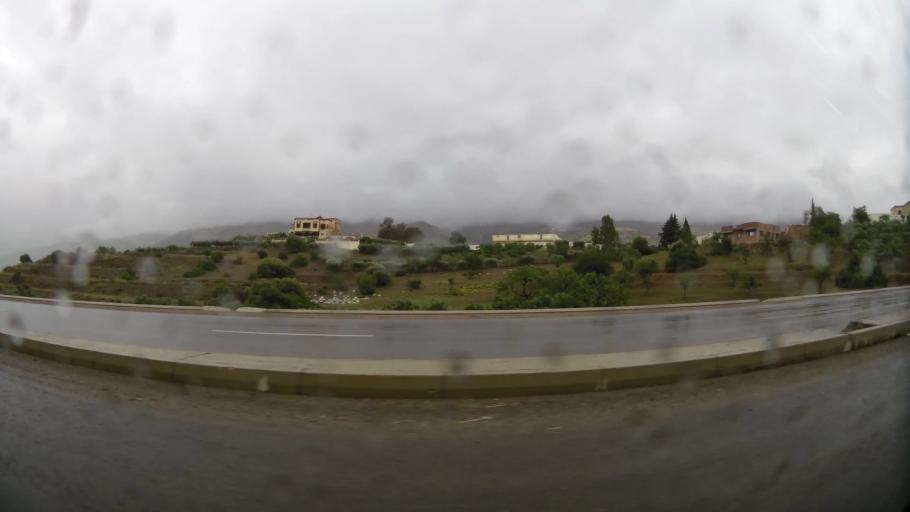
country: MA
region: Taza-Al Hoceima-Taounate
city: Imzourene
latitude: 35.0400
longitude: -3.8213
